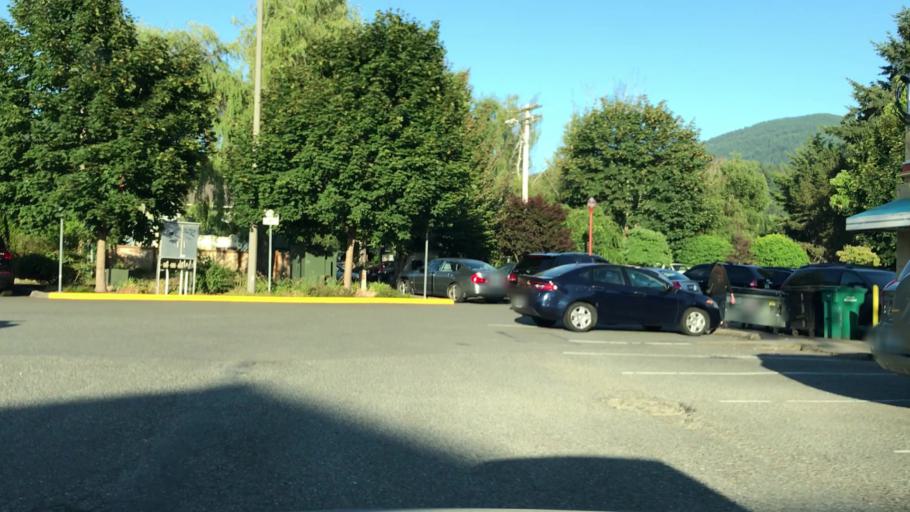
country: US
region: Washington
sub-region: King County
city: Issaquah
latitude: 47.5324
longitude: -122.0363
